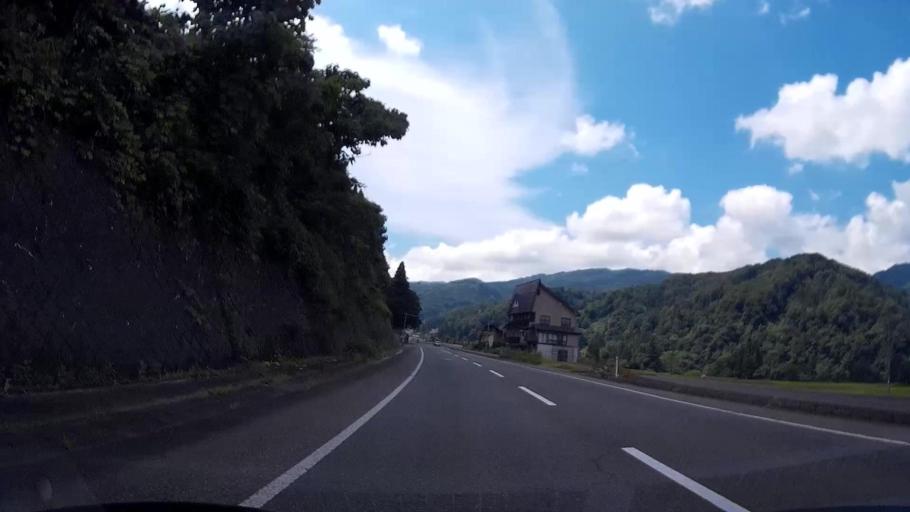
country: JP
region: Niigata
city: Tokamachi
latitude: 36.9952
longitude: 138.6028
